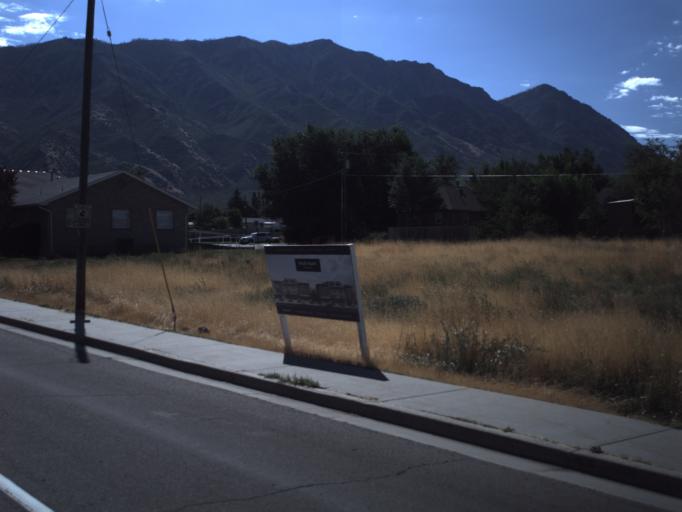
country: US
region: Utah
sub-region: Utah County
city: Santaquin
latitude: 39.9756
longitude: -111.7926
